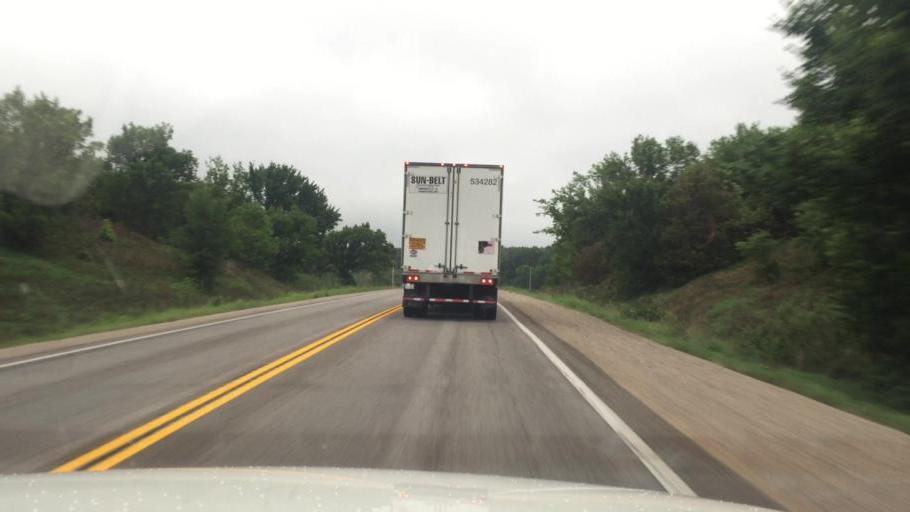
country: US
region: Kansas
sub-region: Montgomery County
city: Cherryvale
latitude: 37.1584
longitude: -95.5768
